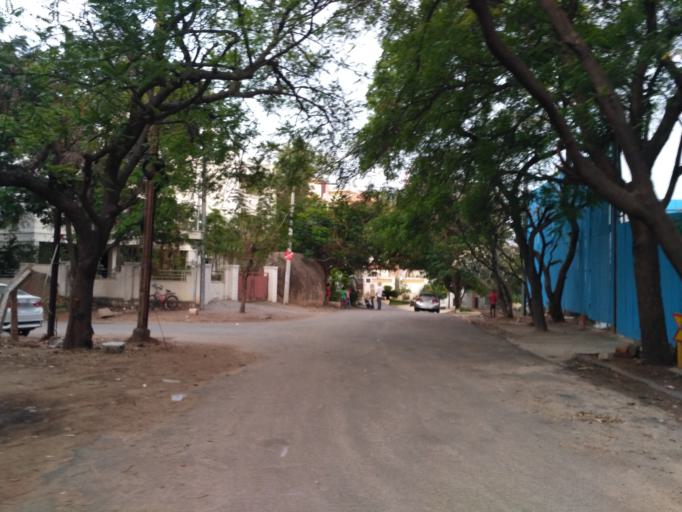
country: IN
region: Telangana
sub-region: Rangareddi
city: Kukatpalli
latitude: 17.4380
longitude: 78.4050
